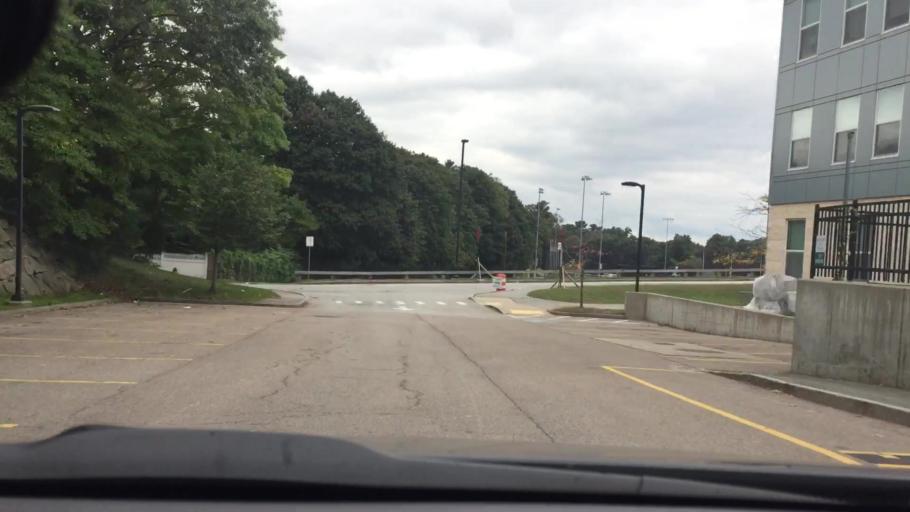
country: US
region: Massachusetts
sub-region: Norfolk County
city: Needham
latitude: 42.2854
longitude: -71.2312
